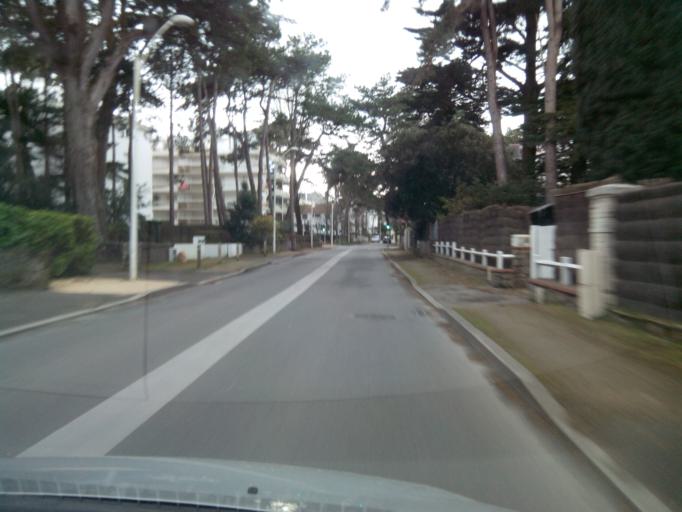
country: FR
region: Pays de la Loire
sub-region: Departement de la Loire-Atlantique
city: Le Pouliguen
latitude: 47.2791
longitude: -2.4164
